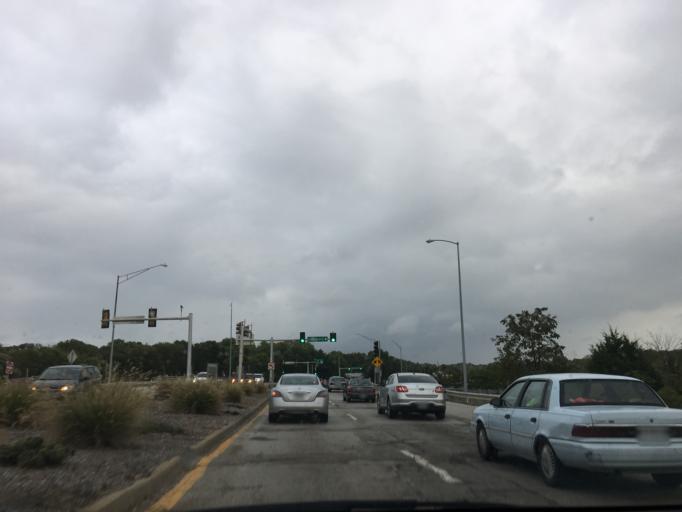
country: US
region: Missouri
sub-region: Saint Louis County
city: Maryland Heights
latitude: 38.7078
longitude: -90.4100
